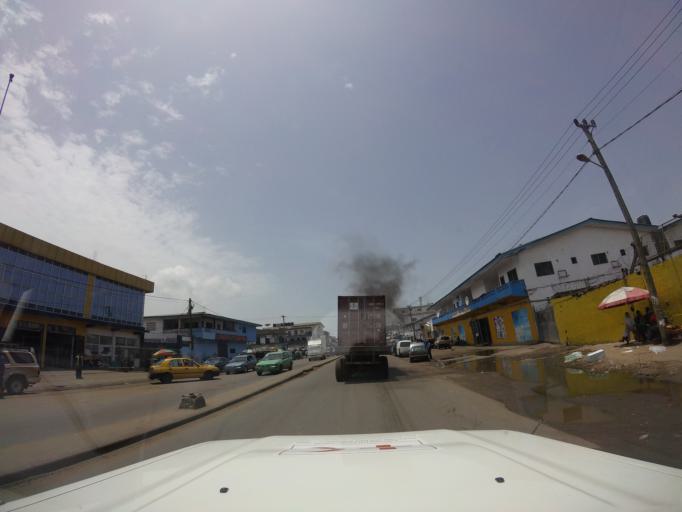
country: LR
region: Montserrado
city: Monrovia
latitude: 6.3306
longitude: -10.7993
